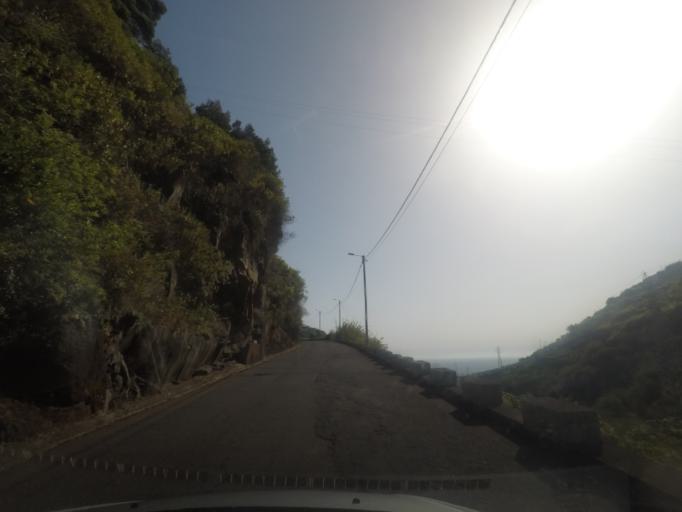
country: PT
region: Madeira
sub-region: Calheta
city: Arco da Calheta
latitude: 32.7301
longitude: -17.1634
